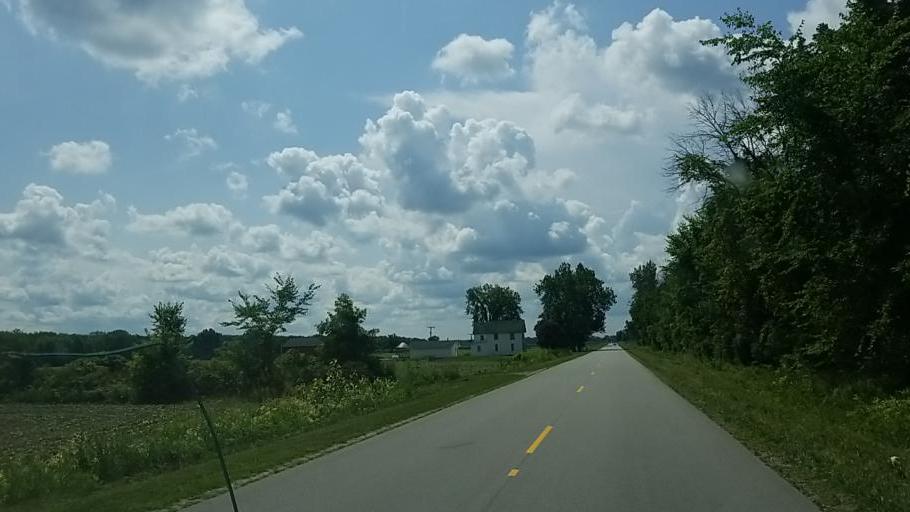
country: US
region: Michigan
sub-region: Muskegon County
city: Ravenna
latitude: 43.1821
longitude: -85.8693
